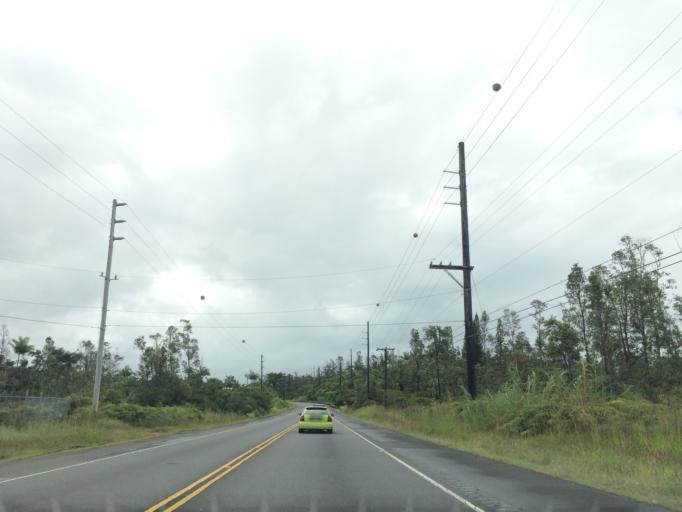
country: US
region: Hawaii
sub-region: Hawaii County
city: Hawaiian Paradise Park
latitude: 19.5147
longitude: -154.9638
